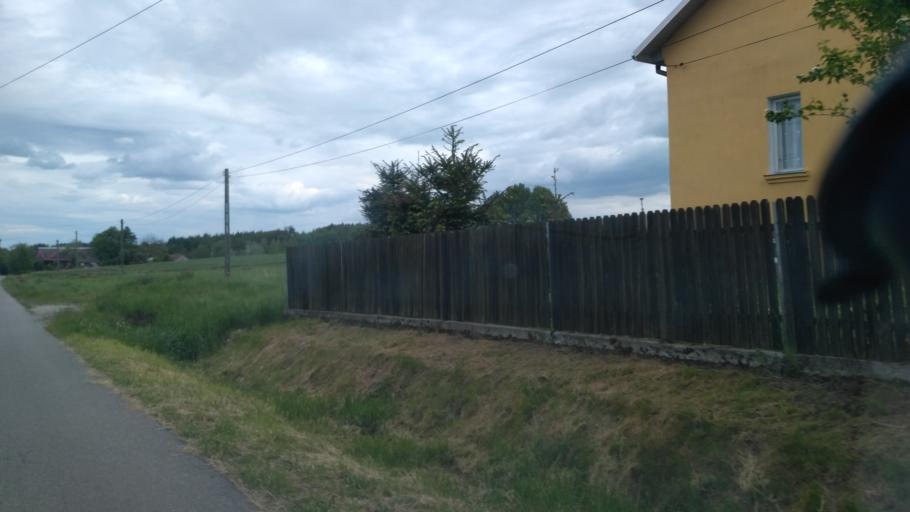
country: PL
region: Subcarpathian Voivodeship
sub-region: Powiat przeworski
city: Jawornik Polski
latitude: 49.8358
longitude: 22.3019
